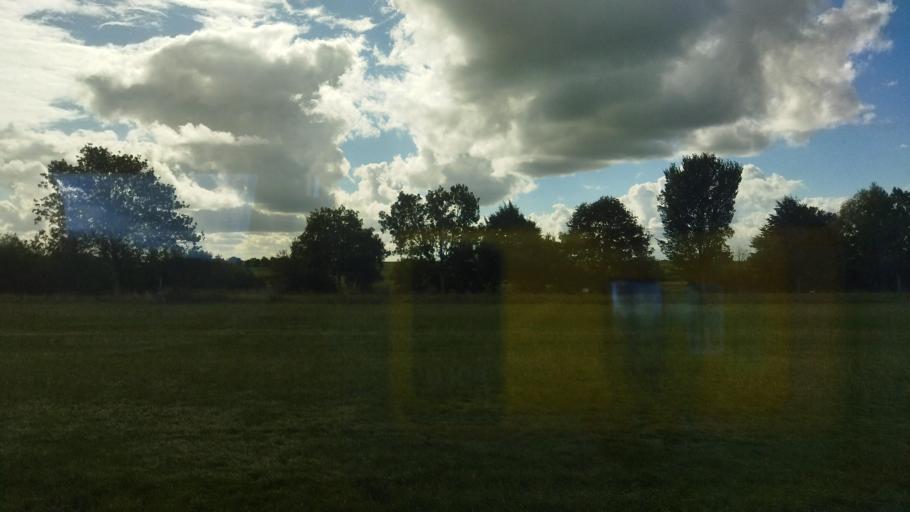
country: DE
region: Lower Saxony
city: Jemgum
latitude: 53.3331
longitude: 7.3291
